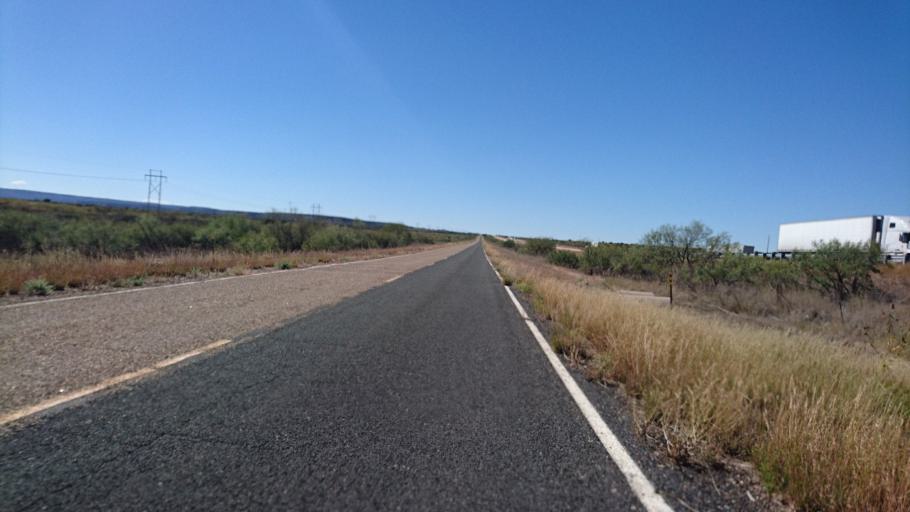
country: US
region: New Mexico
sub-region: Quay County
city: Tucumcari
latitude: 35.0761
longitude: -104.1382
